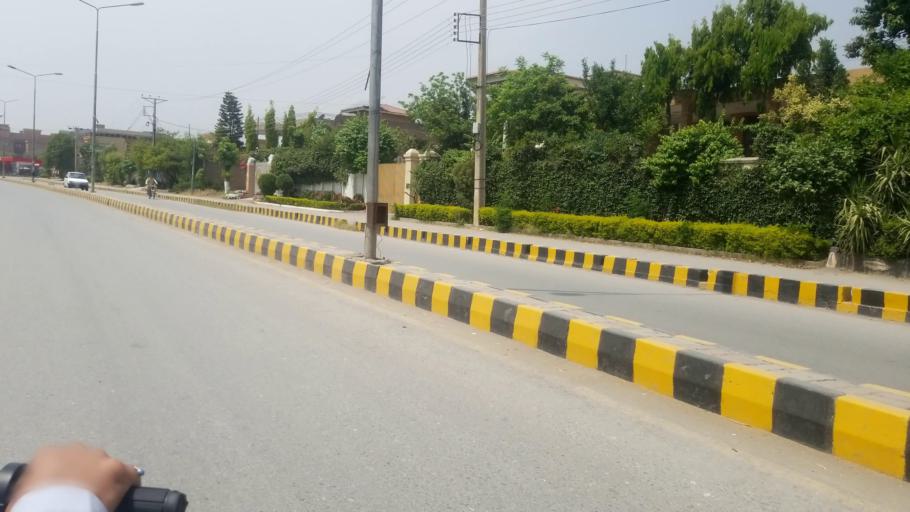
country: PK
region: Khyber Pakhtunkhwa
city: Peshawar
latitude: 33.9942
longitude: 71.4456
